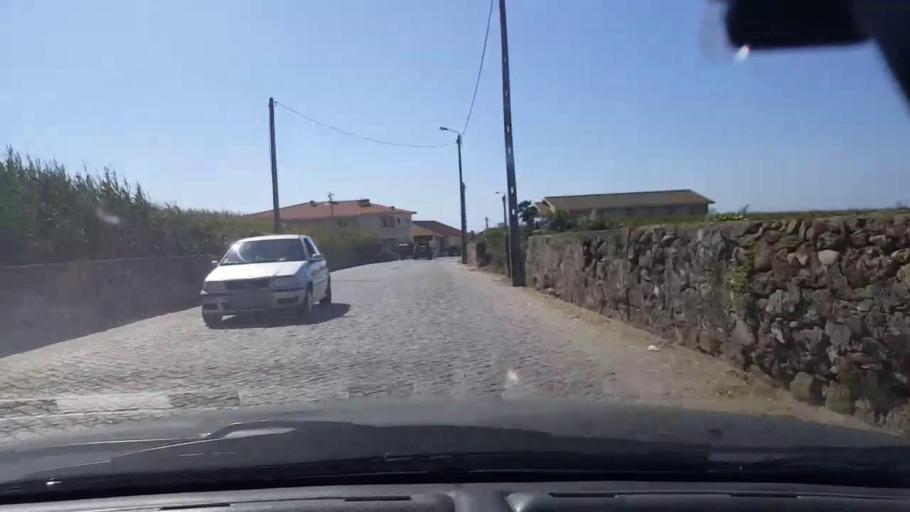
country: PT
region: Porto
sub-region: Matosinhos
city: Lavra
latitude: 41.2919
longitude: -8.7292
